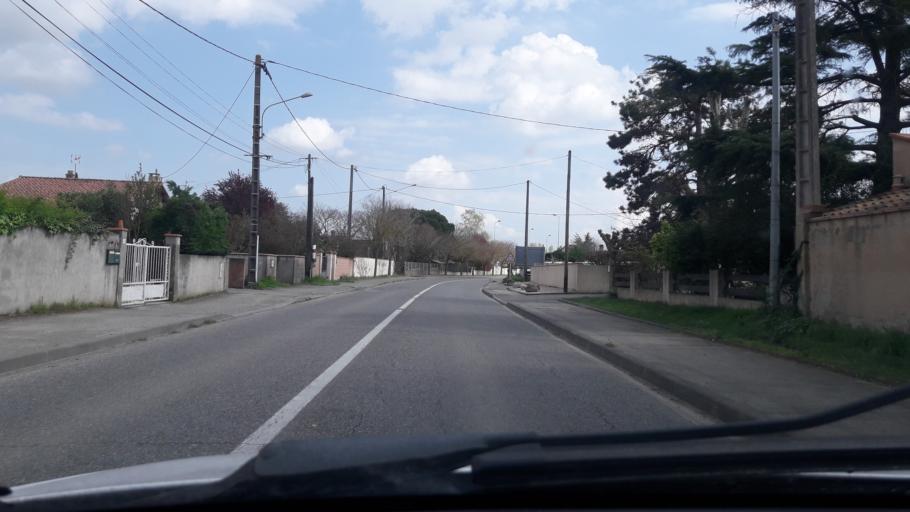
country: FR
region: Midi-Pyrenees
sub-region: Departement de la Haute-Garonne
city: Seysses
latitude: 43.4966
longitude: 1.3017
